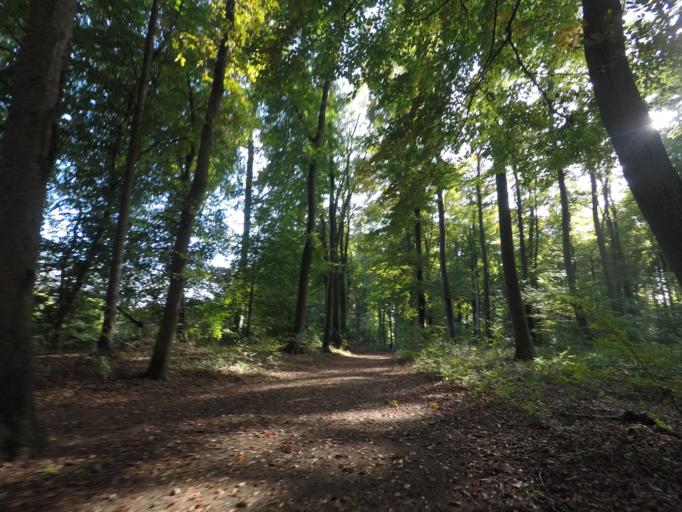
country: LU
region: Luxembourg
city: Itzig
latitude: 49.5952
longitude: 6.1659
